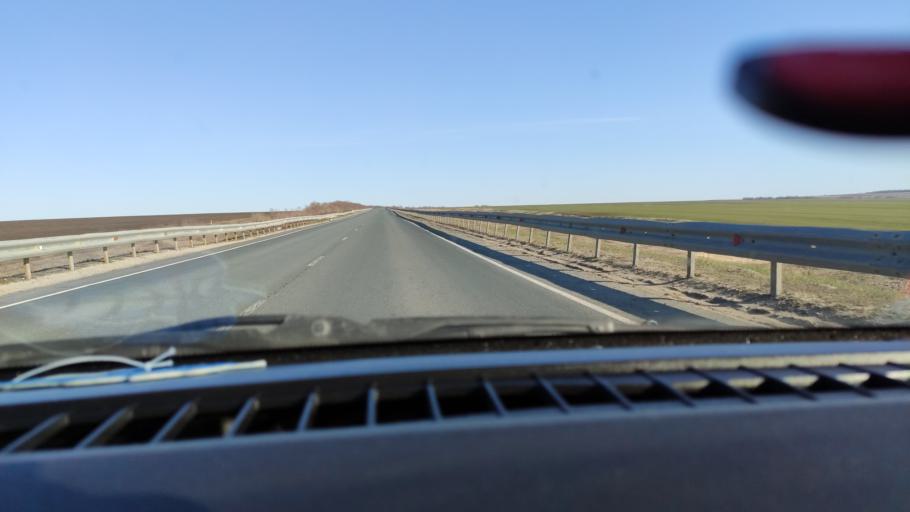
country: RU
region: Saratov
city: Dukhovnitskoye
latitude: 52.7547
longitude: 48.2458
